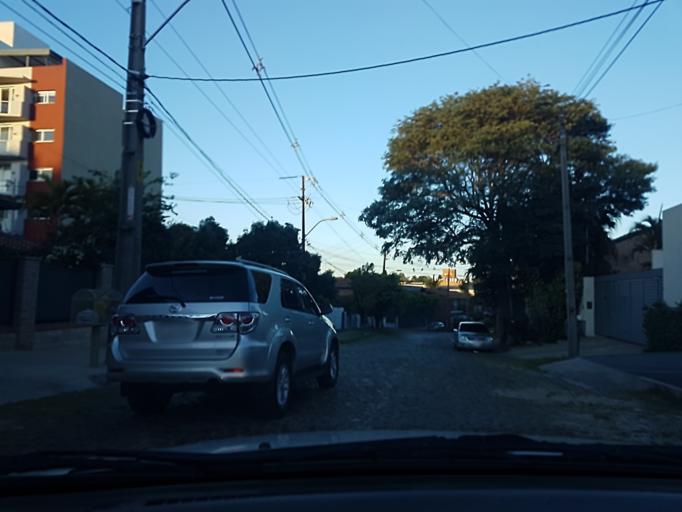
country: PY
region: Asuncion
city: Asuncion
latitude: -25.2738
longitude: -57.5729
